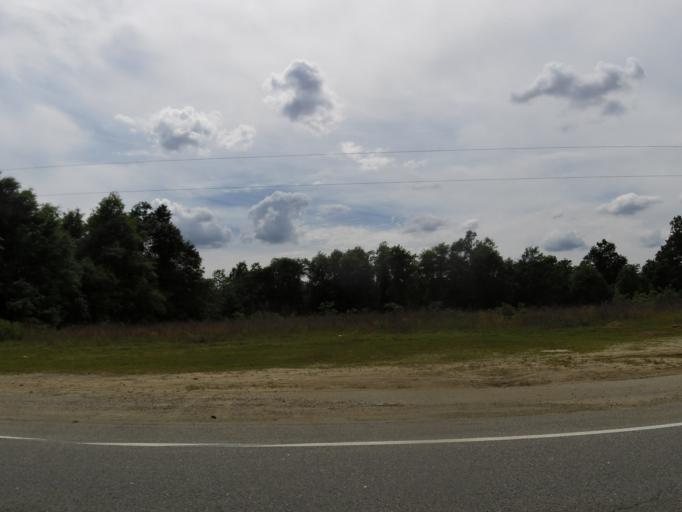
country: US
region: Georgia
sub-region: Jefferson County
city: Louisville
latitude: 33.0927
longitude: -82.4052
